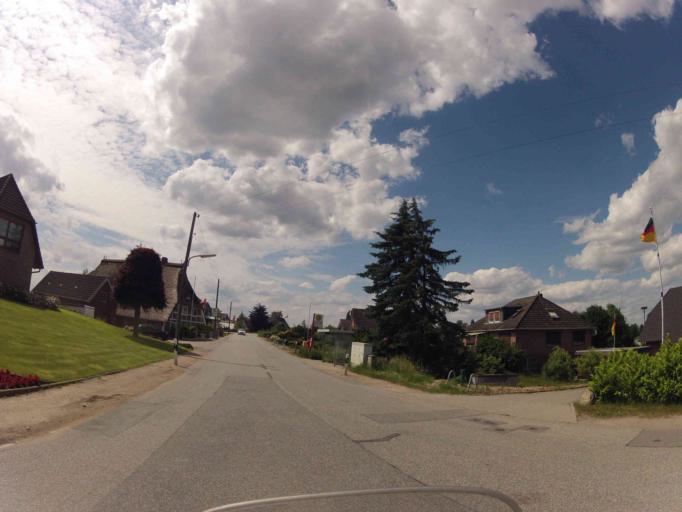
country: DE
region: Hamburg
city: Bergedorf
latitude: 53.4372
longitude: 10.1881
